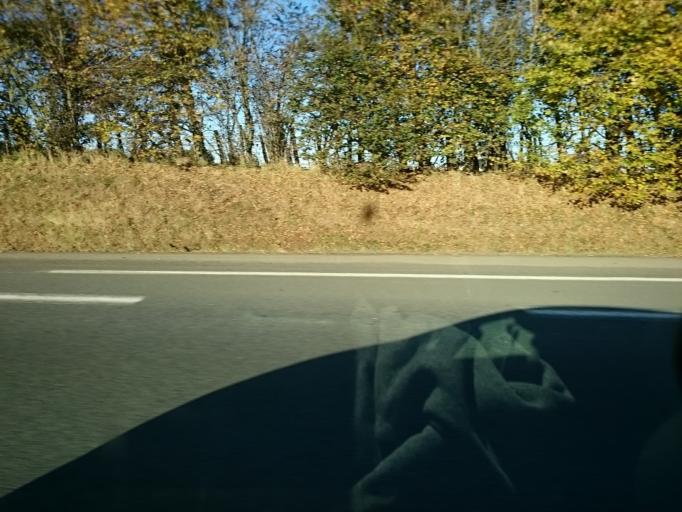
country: FR
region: Brittany
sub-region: Departement des Cotes-d'Armor
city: Broons
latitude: 48.3513
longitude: -2.2938
